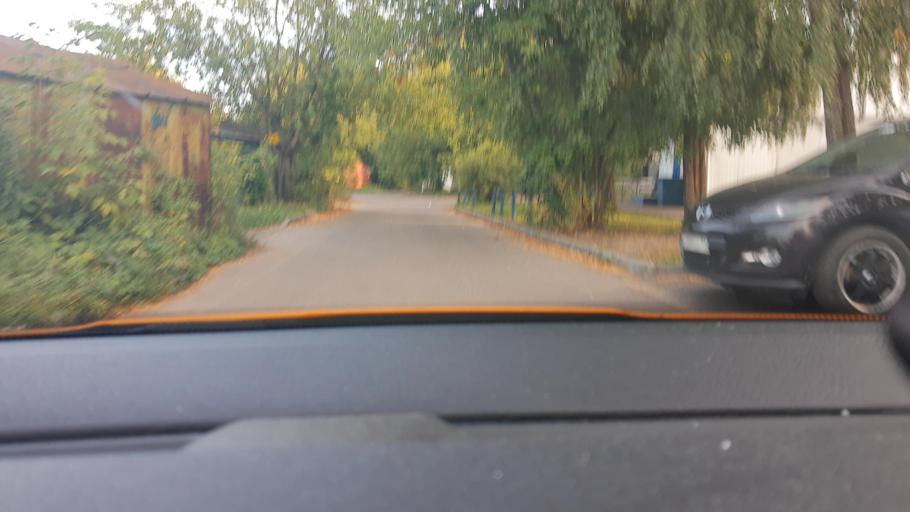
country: RU
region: Moskovskaya
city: Bolshevo
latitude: 55.9524
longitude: 37.8353
